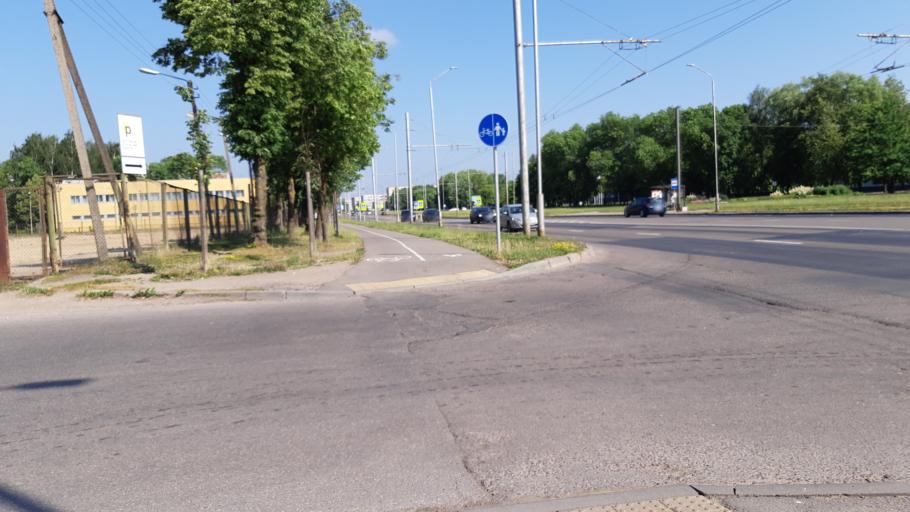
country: LT
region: Kauno apskritis
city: Dainava (Kaunas)
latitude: 54.9189
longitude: 23.9834
